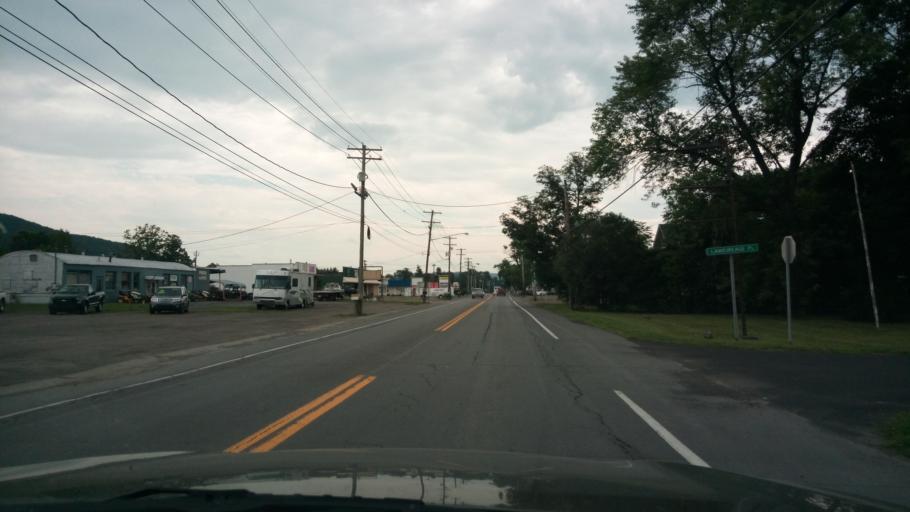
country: US
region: New York
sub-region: Chemung County
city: Elmira Heights
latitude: 42.1258
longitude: -76.8103
